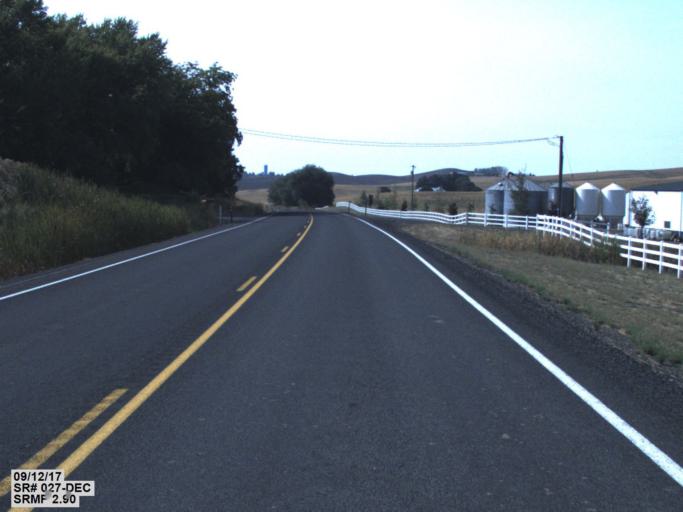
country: US
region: Washington
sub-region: Whitman County
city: Pullman
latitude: 46.7696
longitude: -117.1645
